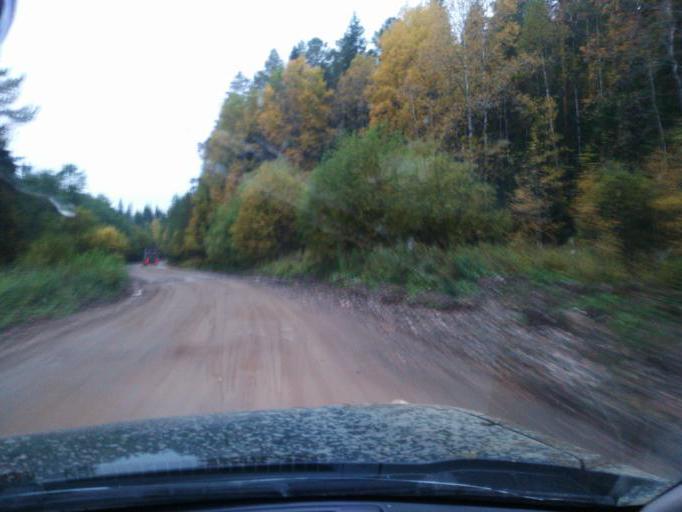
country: RU
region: Sverdlovsk
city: Sylva
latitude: 57.8129
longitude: 58.6040
